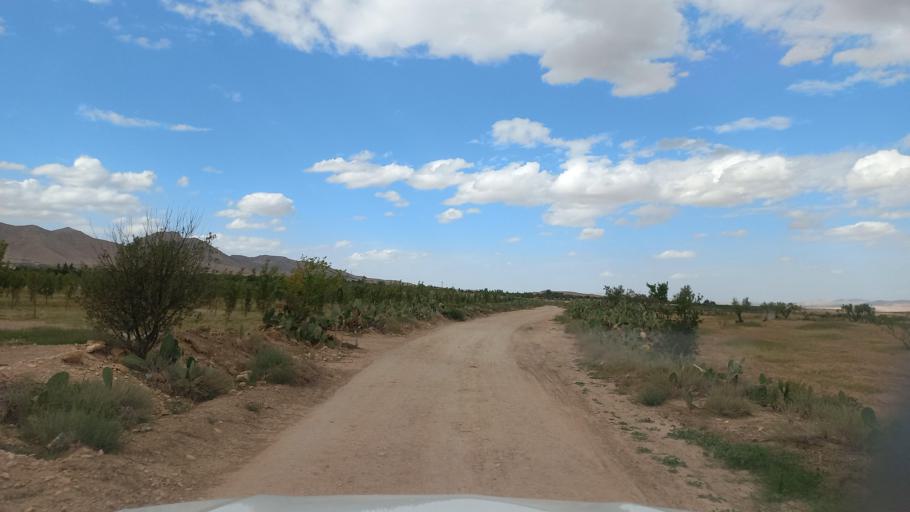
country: TN
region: Al Qasrayn
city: Sbiba
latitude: 35.4328
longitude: 9.0979
